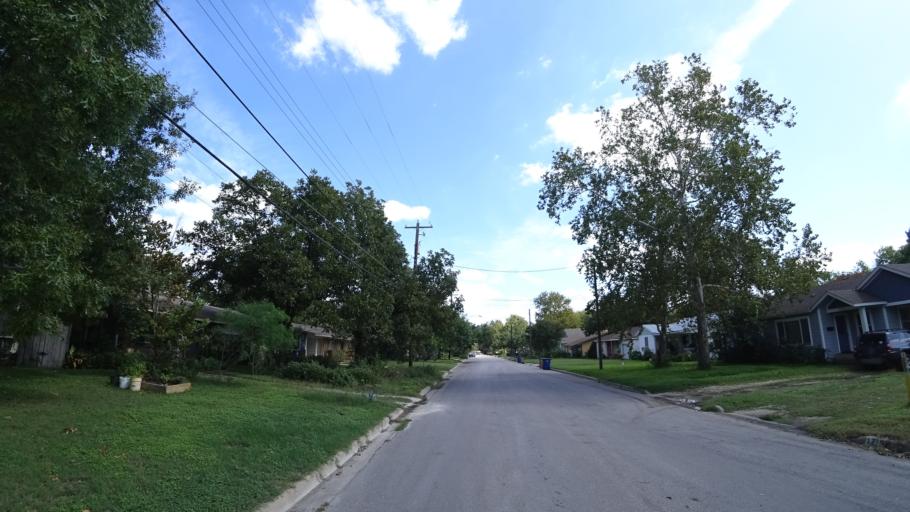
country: US
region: Texas
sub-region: Travis County
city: Austin
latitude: 30.3452
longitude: -97.7293
